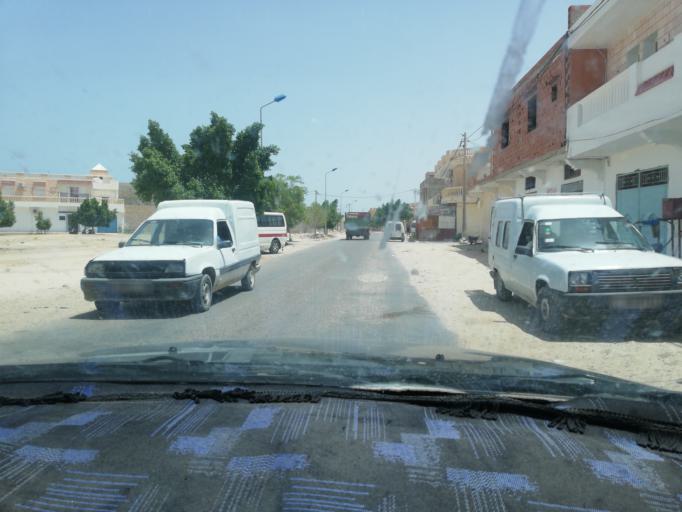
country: TN
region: Qabis
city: Matmata
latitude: 33.6197
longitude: 10.2732
